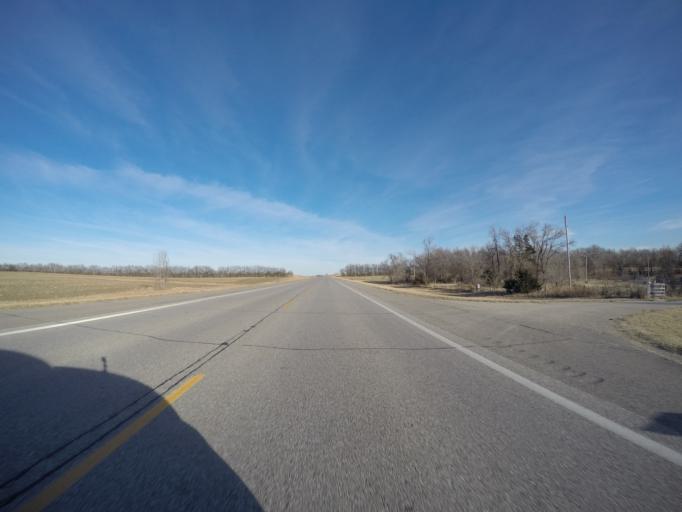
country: US
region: Kansas
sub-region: Marion County
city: Peabody
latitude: 38.1750
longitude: -97.1846
